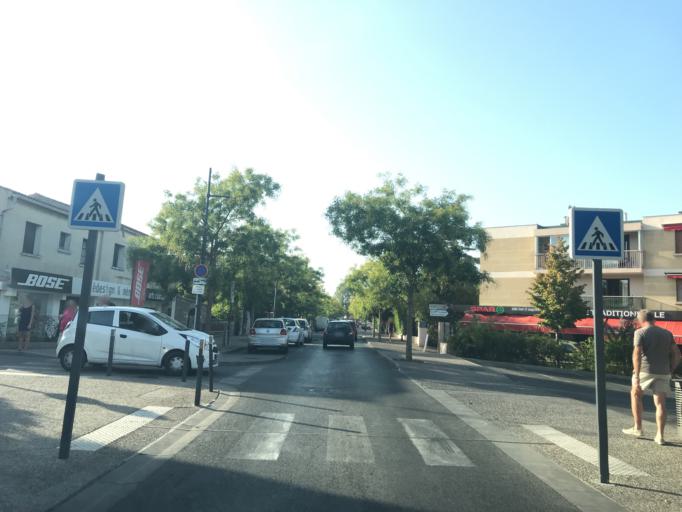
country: FR
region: Provence-Alpes-Cote d'Azur
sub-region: Departement du Var
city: Sanary-sur-Mer
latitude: 43.1146
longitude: 5.8112
